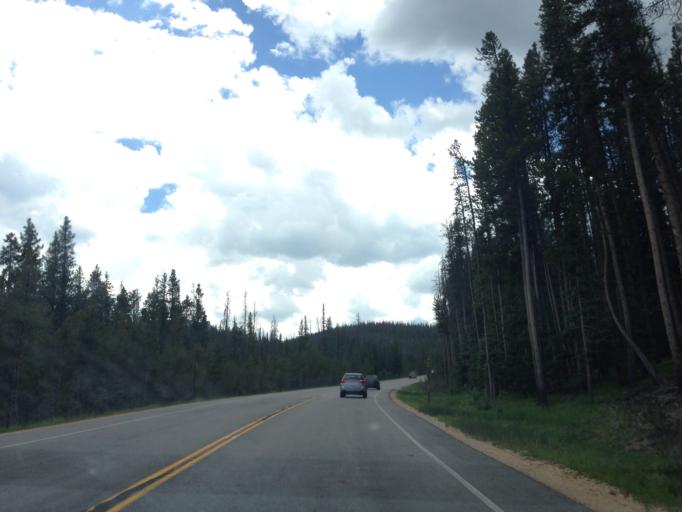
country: US
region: Colorado
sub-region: Larimer County
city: Estes Park
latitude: 40.5890
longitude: -105.8468
